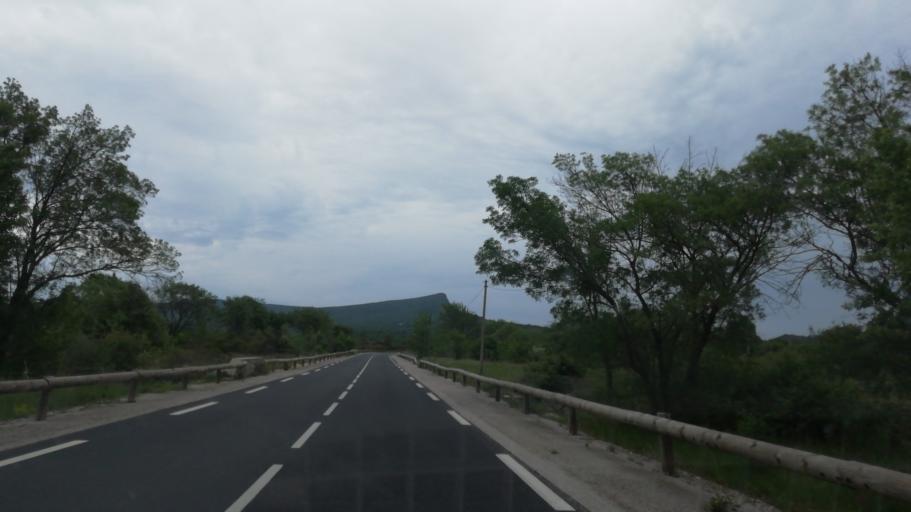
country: FR
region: Languedoc-Roussillon
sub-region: Departement de l'Herault
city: Saint-Martin-de-Londres
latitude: 43.7923
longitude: 3.7890
